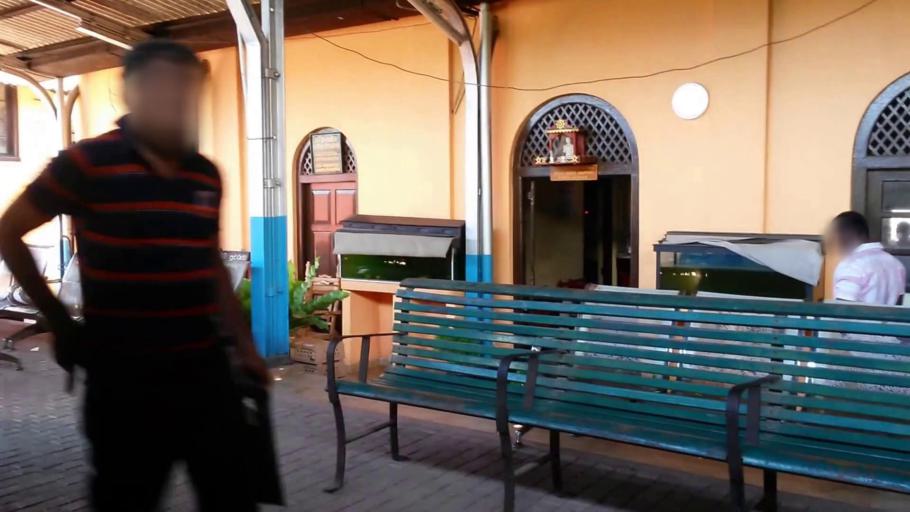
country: LK
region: Southern
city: Hikkaduwa
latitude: 6.1544
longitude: 80.0988
